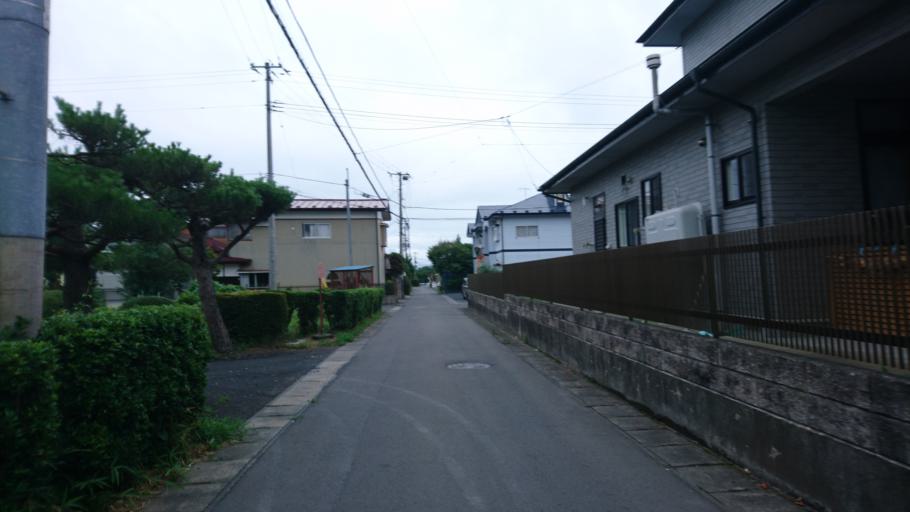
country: JP
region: Iwate
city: Ichinoseki
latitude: 38.9266
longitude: 141.1084
